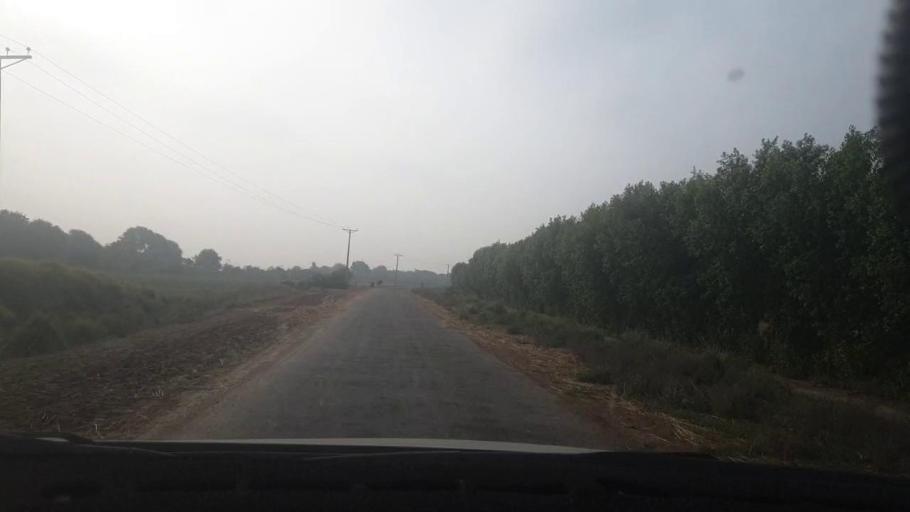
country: PK
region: Sindh
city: Tando Muhammad Khan
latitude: 25.0984
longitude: 68.5160
